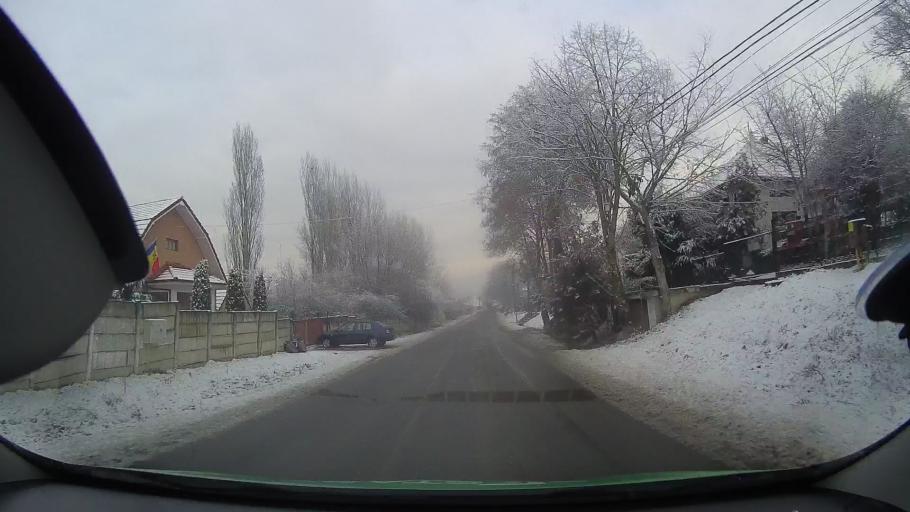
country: RO
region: Mures
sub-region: Comuna Bogata
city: Bogata
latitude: 46.4624
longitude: 24.0823
